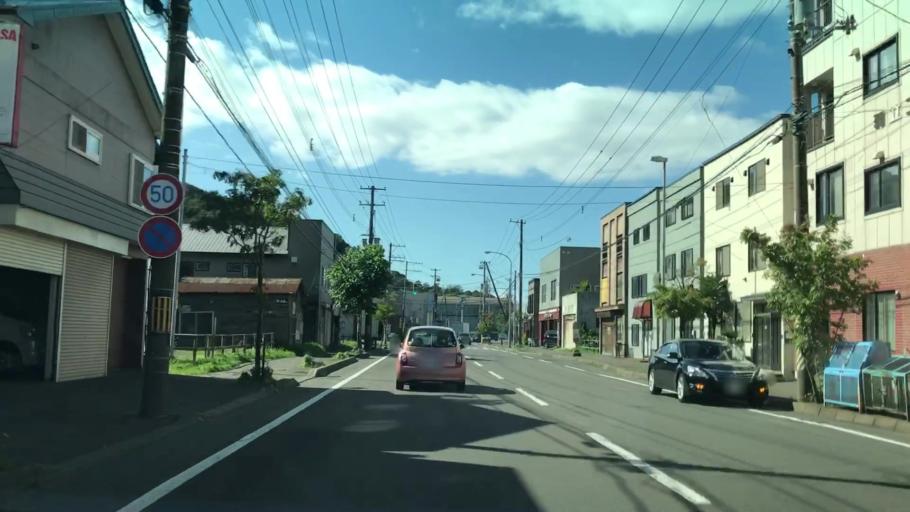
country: JP
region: Hokkaido
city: Muroran
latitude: 42.3346
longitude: 140.9602
